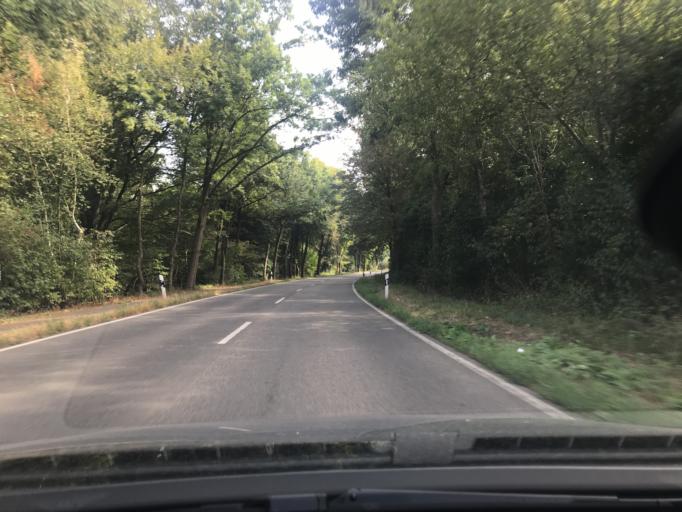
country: DE
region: North Rhine-Westphalia
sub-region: Regierungsbezirk Dusseldorf
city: Grefrath
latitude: 51.3496
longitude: 6.3736
